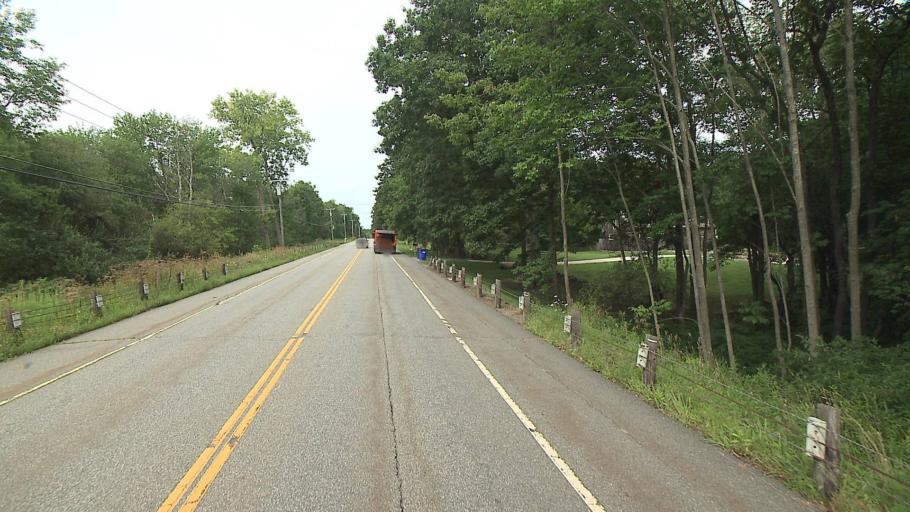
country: US
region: Connecticut
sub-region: Litchfield County
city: New Preston
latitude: 41.7439
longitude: -73.3707
